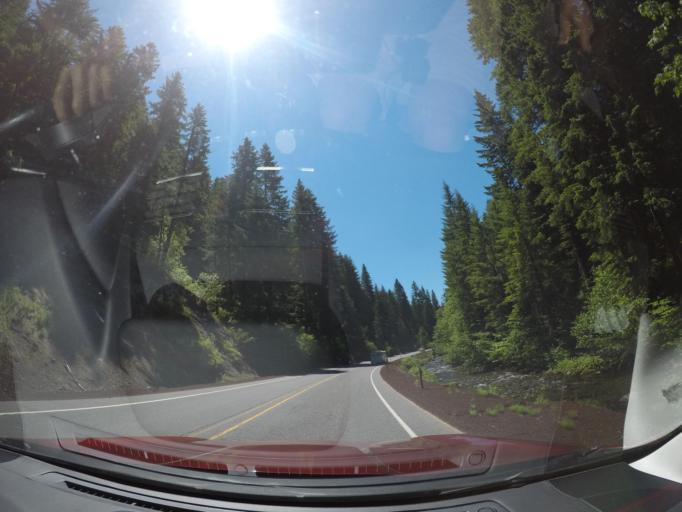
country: US
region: Oregon
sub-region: Deschutes County
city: Sisters
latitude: 44.5466
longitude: -121.9941
